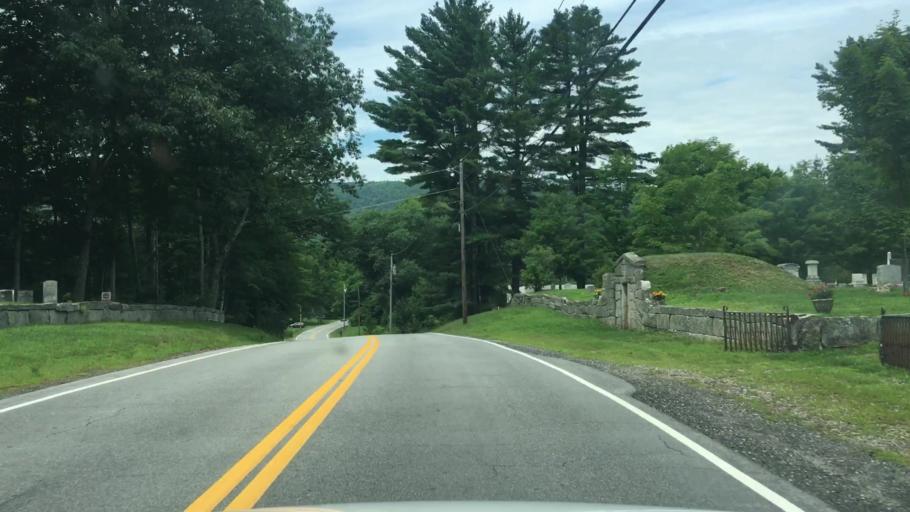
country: US
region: New Hampshire
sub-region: Grafton County
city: Rumney
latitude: 43.8020
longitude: -71.8041
